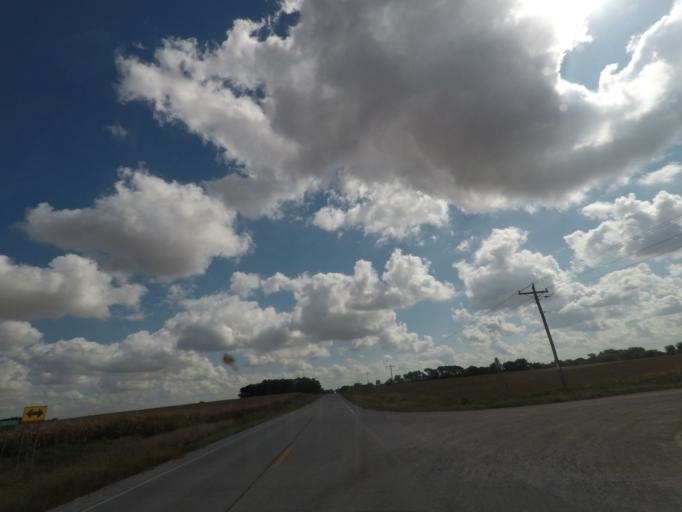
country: US
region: Iowa
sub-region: Story County
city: Nevada
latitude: 42.0226
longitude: -93.3575
